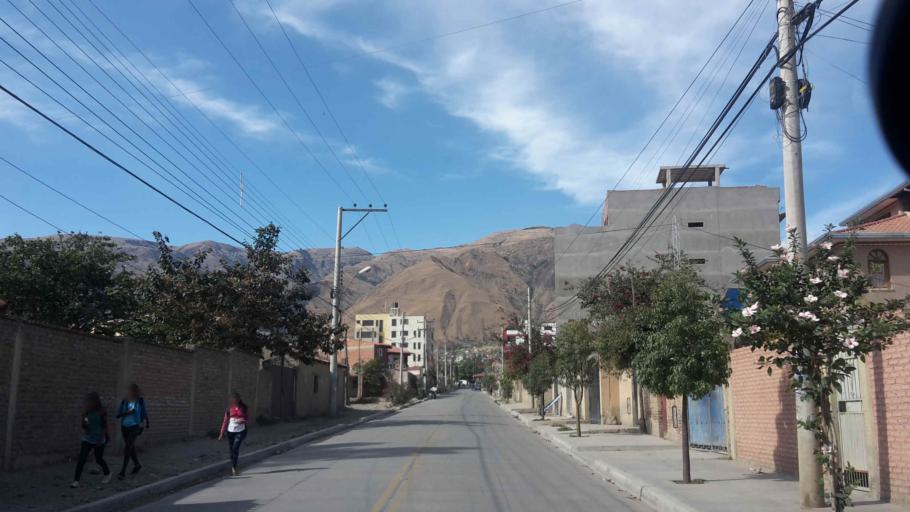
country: BO
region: Cochabamba
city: Cochabamba
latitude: -17.3476
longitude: -66.2049
